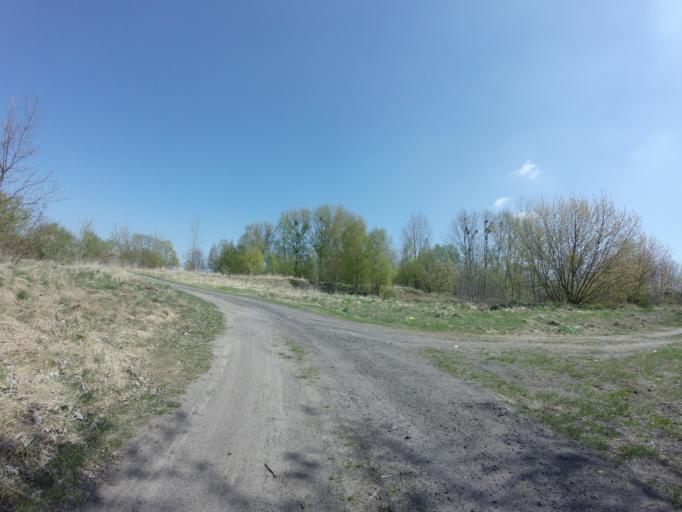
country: PL
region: West Pomeranian Voivodeship
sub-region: Powiat choszczenski
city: Choszczno
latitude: 53.1661
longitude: 15.4463
